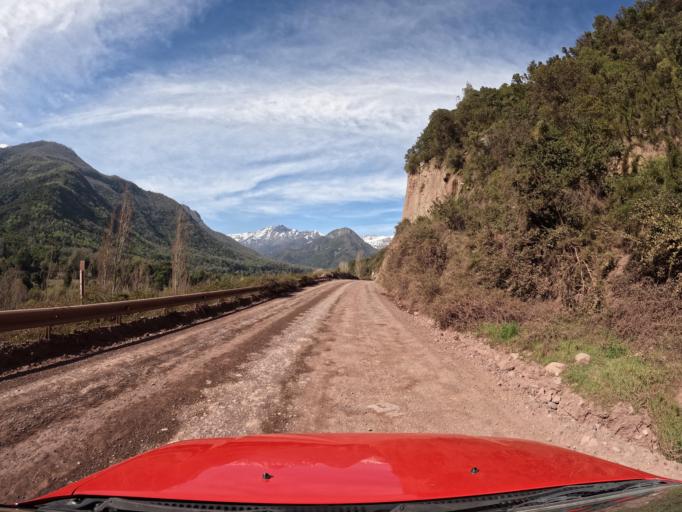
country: CL
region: O'Higgins
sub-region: Provincia de Colchagua
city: Chimbarongo
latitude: -35.0006
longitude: -70.7914
